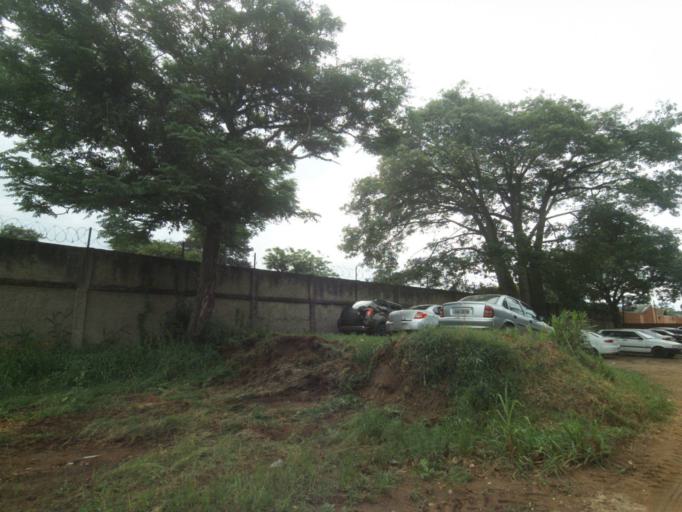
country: BR
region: Parana
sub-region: Pinhais
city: Pinhais
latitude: -25.4252
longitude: -49.2228
